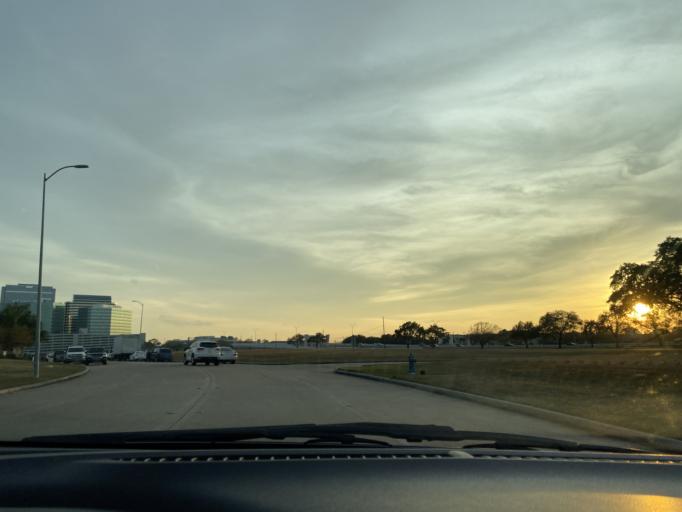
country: US
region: Texas
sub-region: Harris County
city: Bunker Hill Village
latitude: 29.7350
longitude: -95.5553
